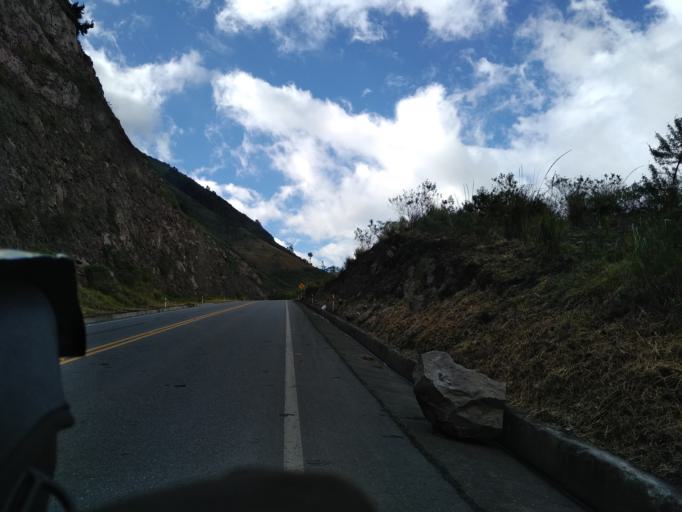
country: EC
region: Tungurahua
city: Banos
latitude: -1.4830
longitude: -78.5186
